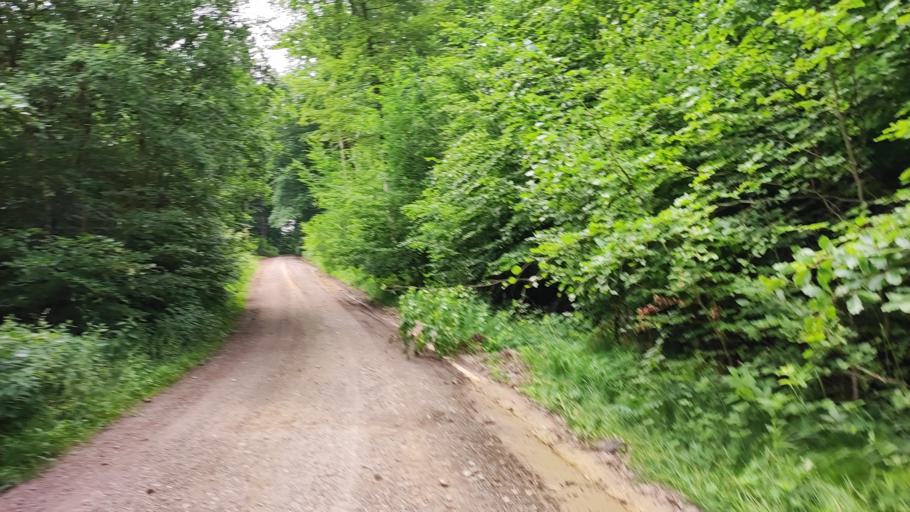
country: DE
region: Bavaria
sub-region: Swabia
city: Adelsried
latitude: 48.4161
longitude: 10.7042
